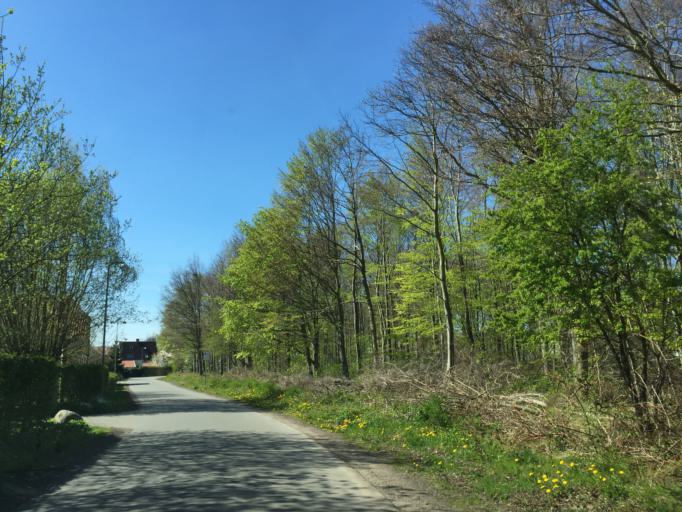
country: DK
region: South Denmark
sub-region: Odense Kommune
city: Odense
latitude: 55.3712
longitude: 10.4015
